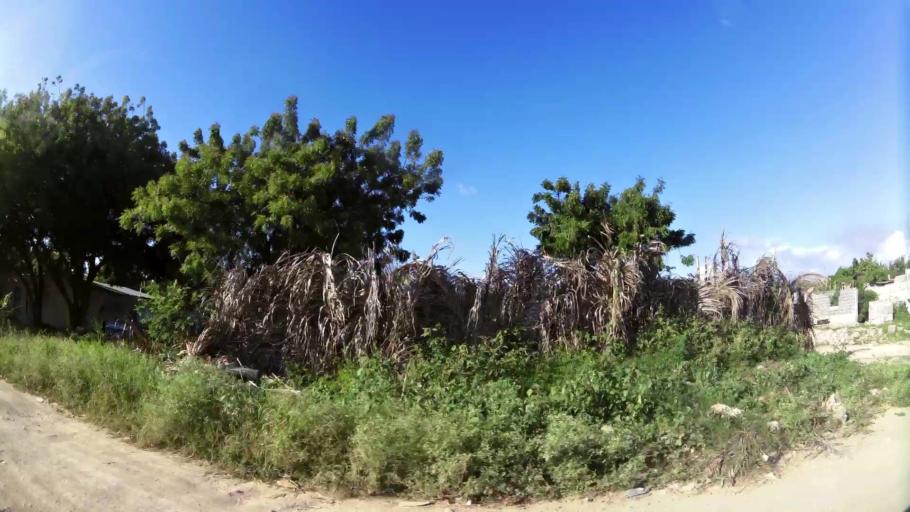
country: DO
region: Santo Domingo
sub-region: Santo Domingo
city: Santo Domingo Este
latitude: 18.4759
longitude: -69.8119
